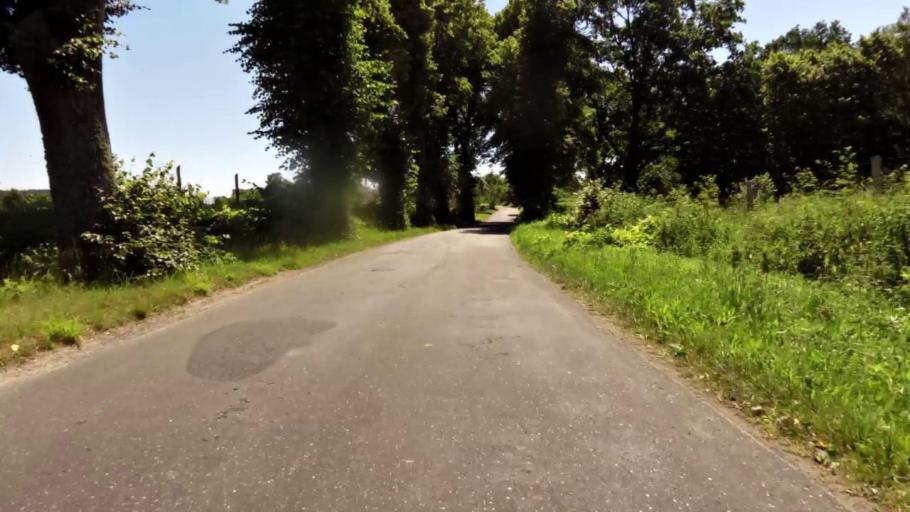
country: PL
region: West Pomeranian Voivodeship
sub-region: Powiat swidwinski
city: Polczyn-Zdroj
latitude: 53.9003
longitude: 16.0854
